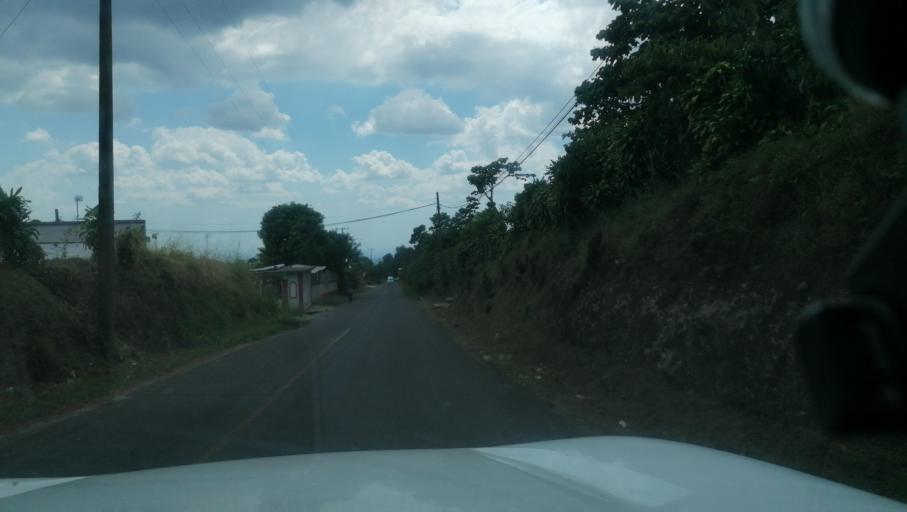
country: MX
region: Chiapas
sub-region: Cacahoatan
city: Benito Juarez
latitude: 15.0401
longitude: -92.1526
